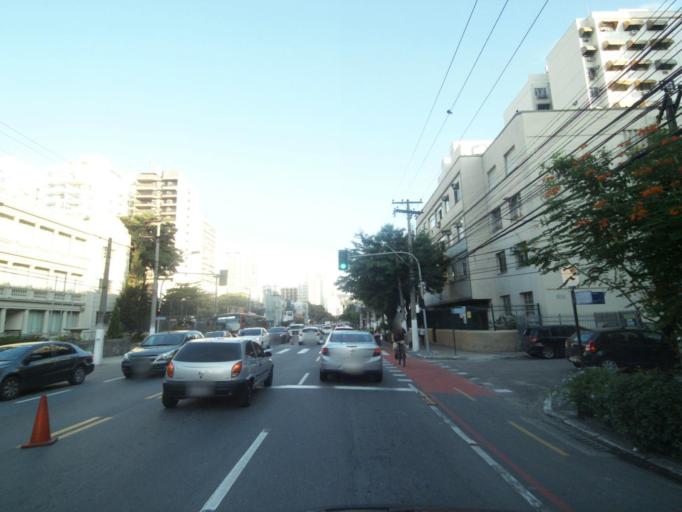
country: BR
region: Rio de Janeiro
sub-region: Niteroi
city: Niteroi
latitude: -22.9004
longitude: -43.1098
